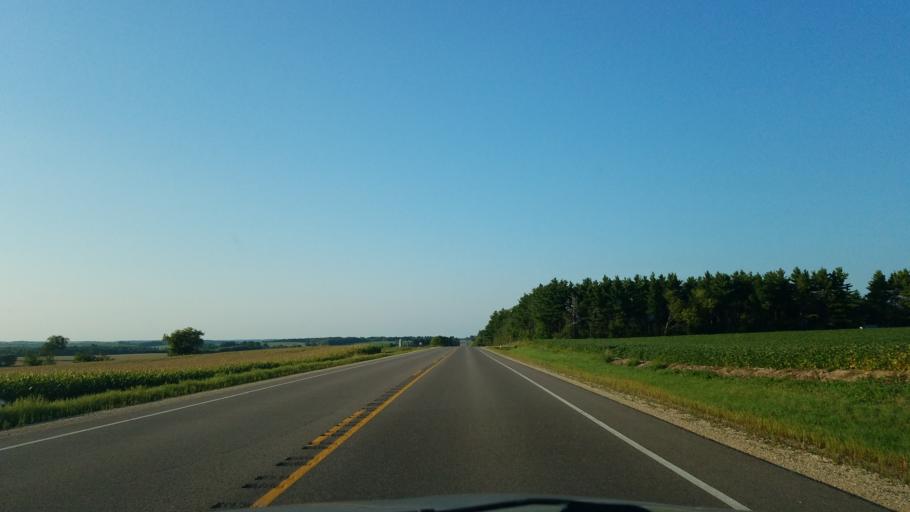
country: US
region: Wisconsin
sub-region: Saint Croix County
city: Baldwin
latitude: 45.0917
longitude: -92.3754
